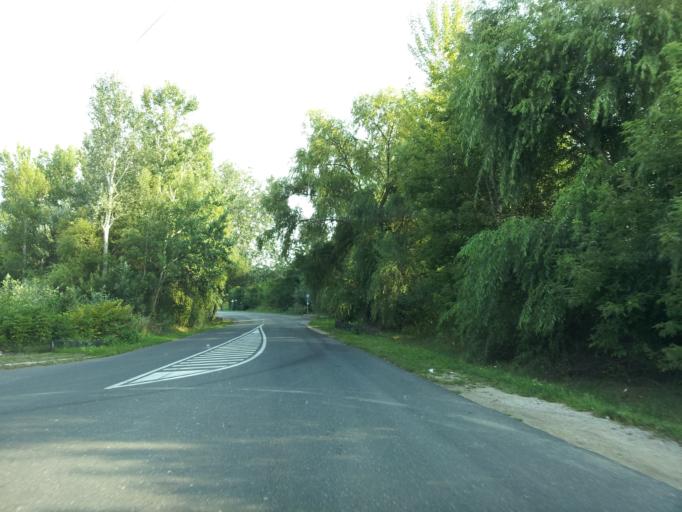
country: HU
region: Somogy
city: Zamardi
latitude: 46.8930
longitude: 18.0007
